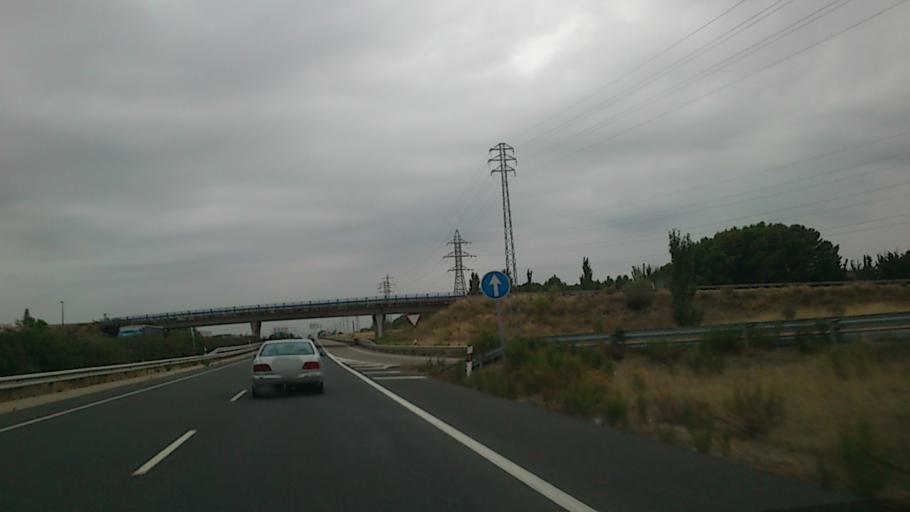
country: ES
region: Aragon
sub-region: Provincia de Zaragoza
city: Villanueva de Gallego
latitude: 41.7297
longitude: -0.8505
